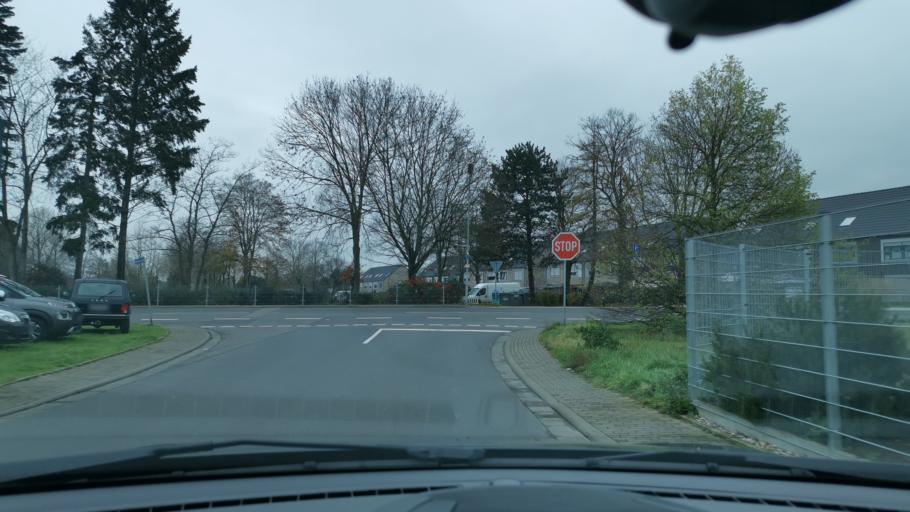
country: DE
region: North Rhine-Westphalia
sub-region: Regierungsbezirk Dusseldorf
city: Neubrueck
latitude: 51.1105
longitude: 6.6307
